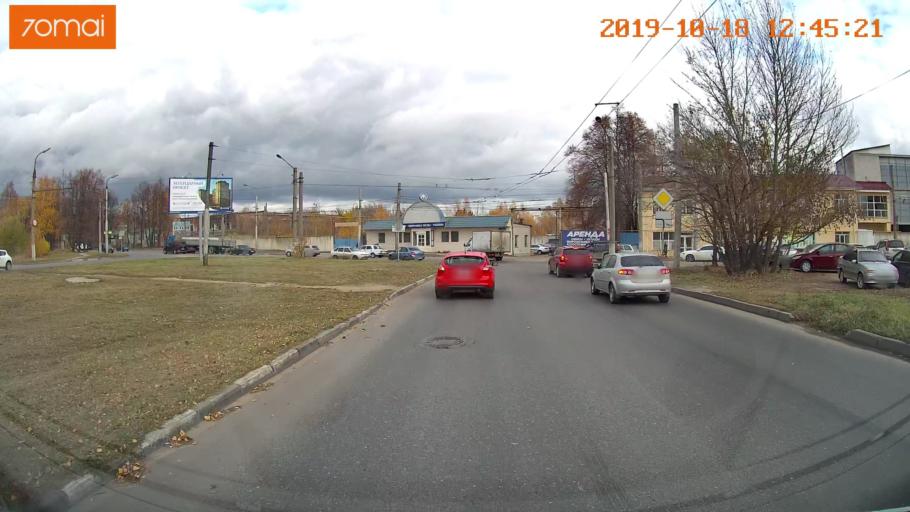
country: RU
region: Rjazan
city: Ryazan'
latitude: 54.6519
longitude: 39.6659
